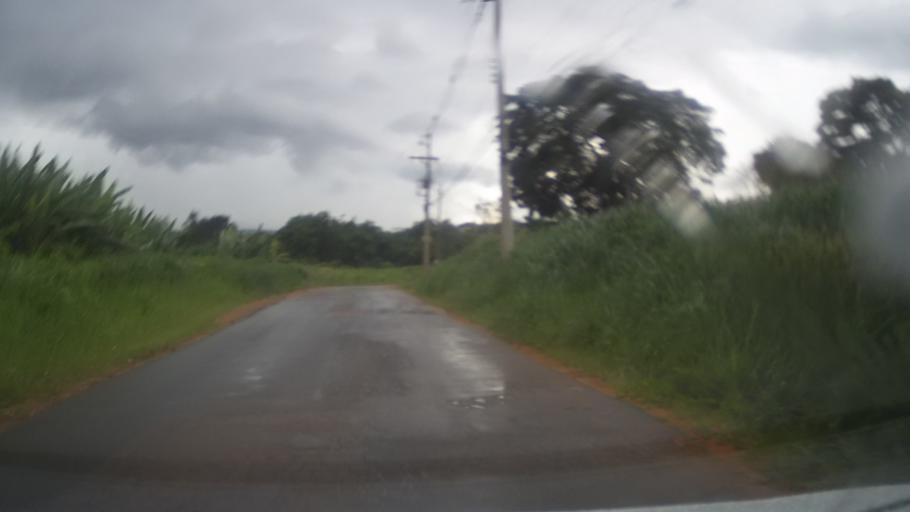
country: BR
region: Sao Paulo
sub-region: Itupeva
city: Itupeva
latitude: -23.1745
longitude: -47.0212
